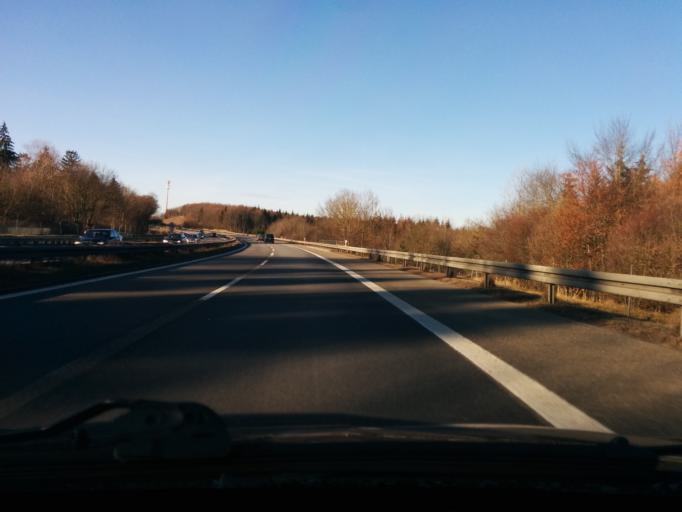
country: DE
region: Bavaria
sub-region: Upper Bavaria
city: Wessling
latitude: 48.0931
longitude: 11.2461
